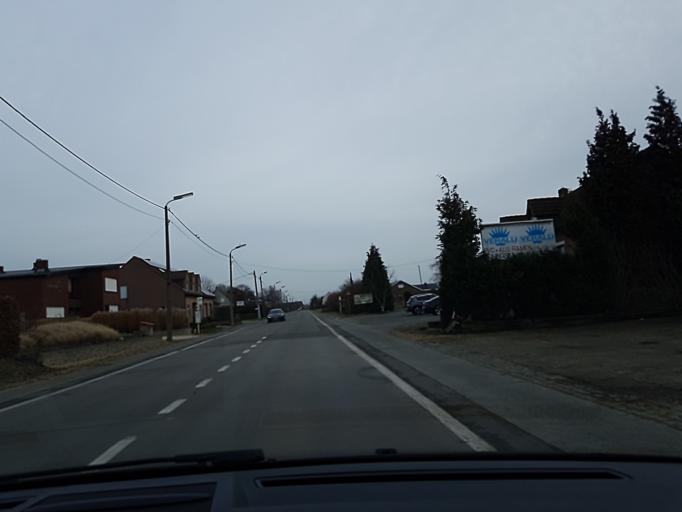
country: BE
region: Flanders
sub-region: Provincie Antwerpen
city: Putte
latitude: 51.0647
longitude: 4.6004
